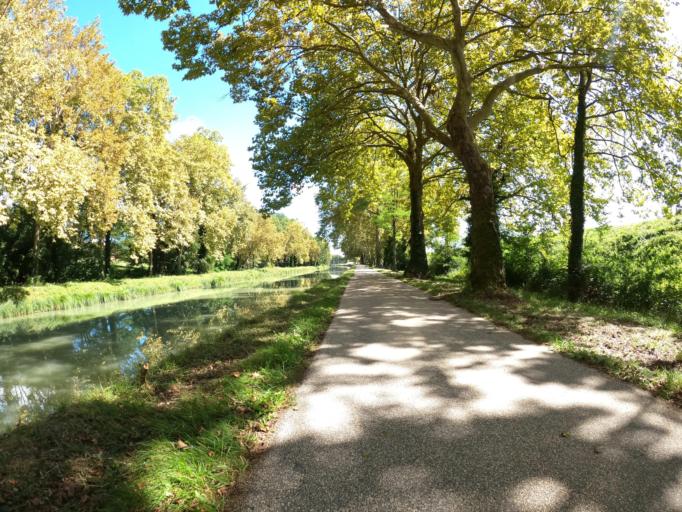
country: FR
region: Midi-Pyrenees
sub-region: Departement du Tarn-et-Garonne
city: Valence
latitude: 44.1011
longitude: 0.9115
